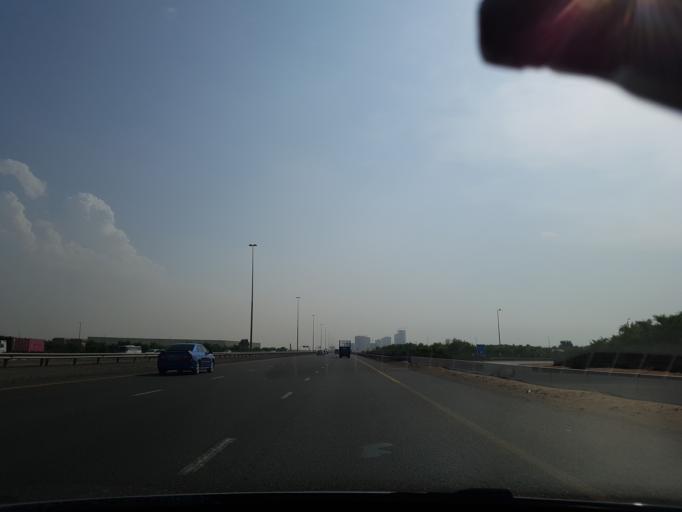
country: AE
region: Umm al Qaywayn
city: Umm al Qaywayn
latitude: 25.4247
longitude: 55.5921
